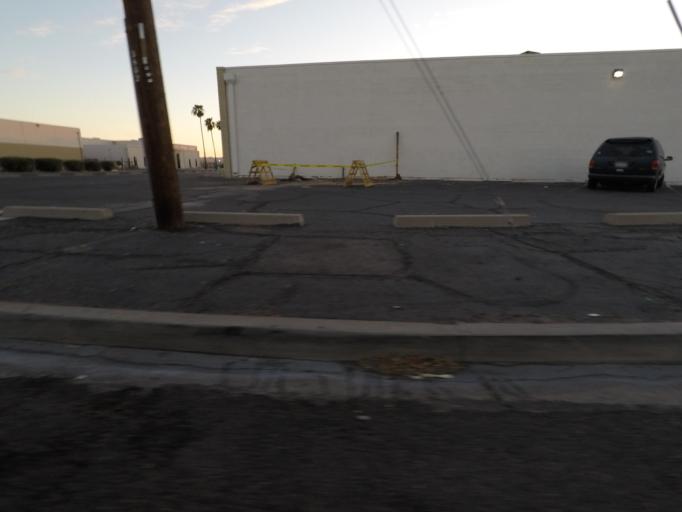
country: US
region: Arizona
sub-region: Maricopa County
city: Glendale
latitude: 33.4912
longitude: -112.1321
